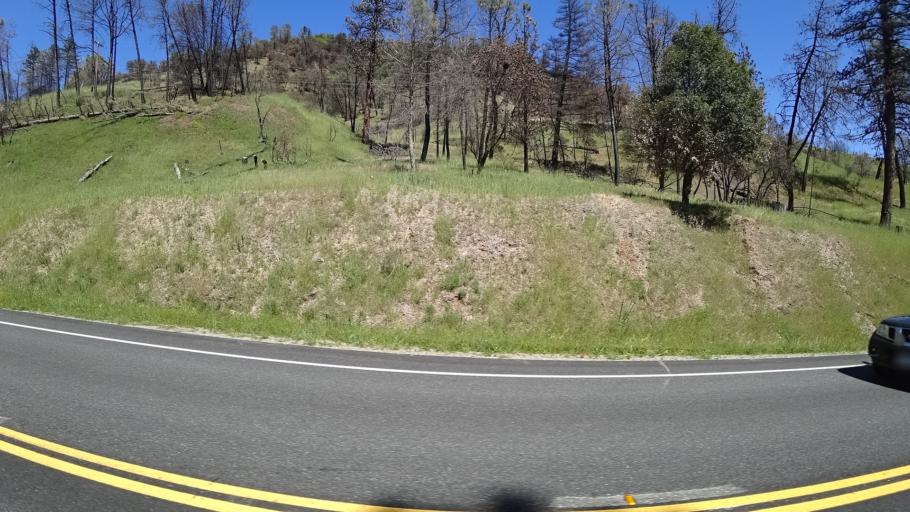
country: US
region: California
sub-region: Trinity County
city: Weaverville
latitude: 40.7702
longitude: -123.1240
